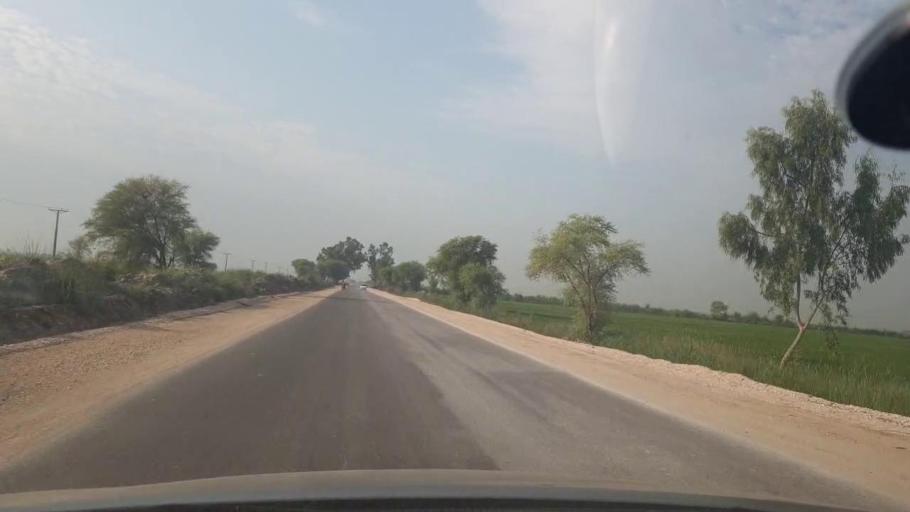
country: PK
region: Sindh
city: Jacobabad
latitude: 28.1861
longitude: 68.3675
